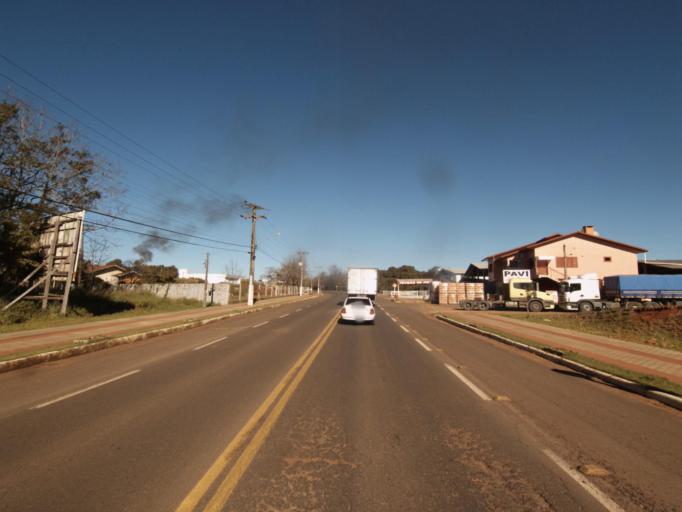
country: AR
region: Misiones
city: Bernardo de Irigoyen
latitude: -26.7588
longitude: -53.5029
